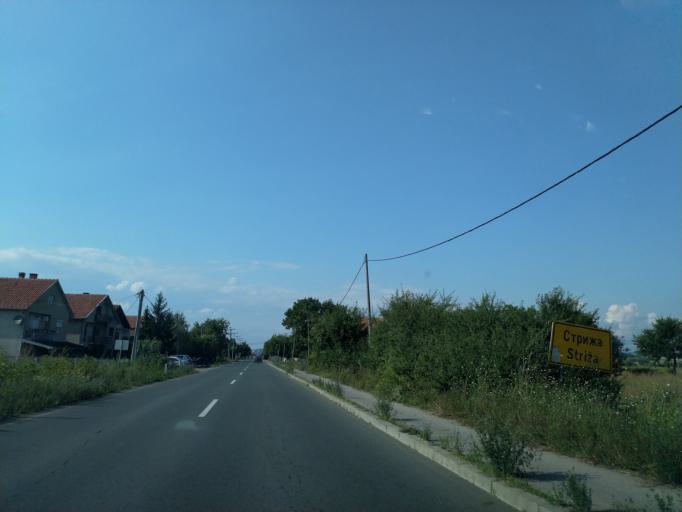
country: RS
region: Central Serbia
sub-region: Pomoravski Okrug
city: Paracin
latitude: 43.8279
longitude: 21.4174
